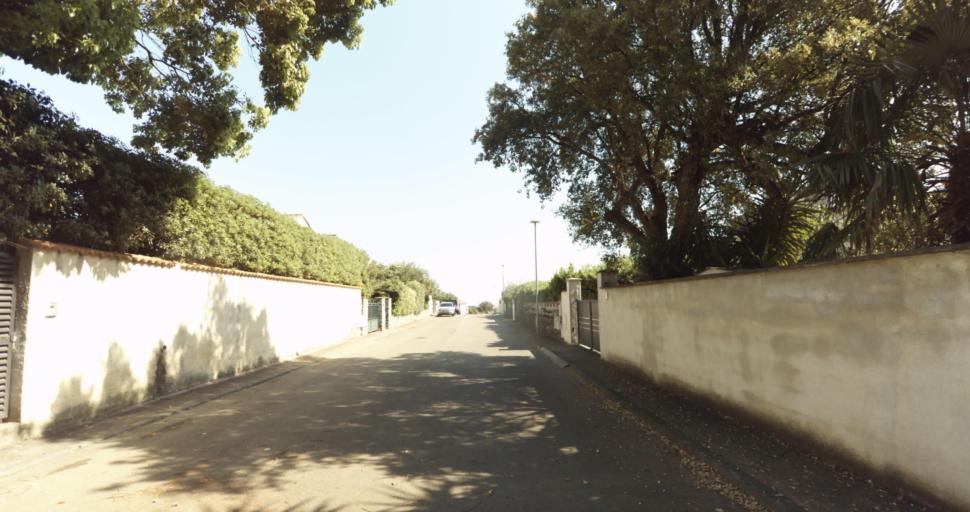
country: FR
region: Corsica
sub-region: Departement de la Haute-Corse
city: Biguglia
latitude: 42.6258
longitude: 9.4271
